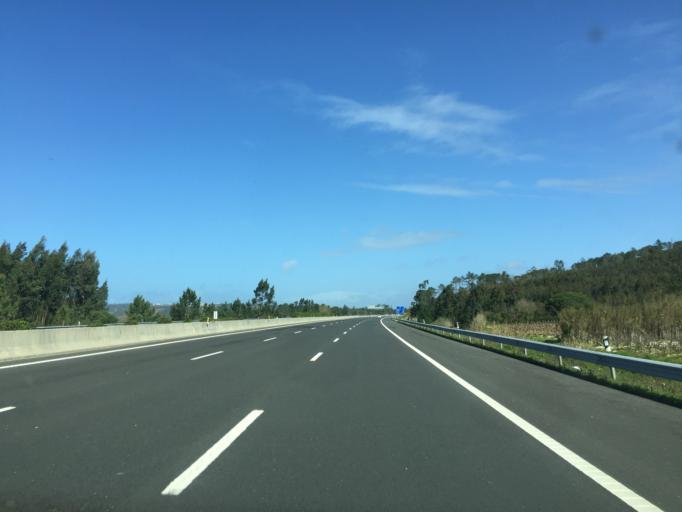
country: PT
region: Leiria
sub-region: Nazare
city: Nazare
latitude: 39.5097
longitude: -9.0893
